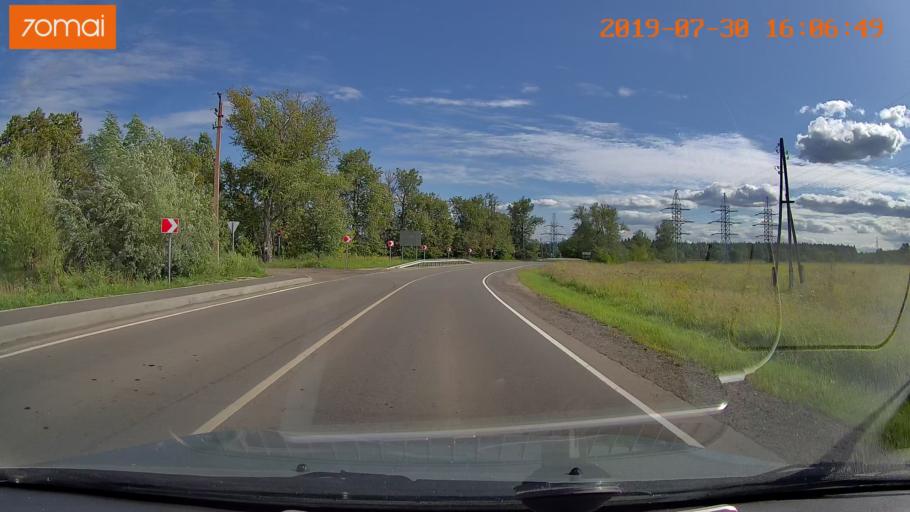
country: RU
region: Moskovskaya
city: Peski
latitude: 55.2523
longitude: 38.7194
